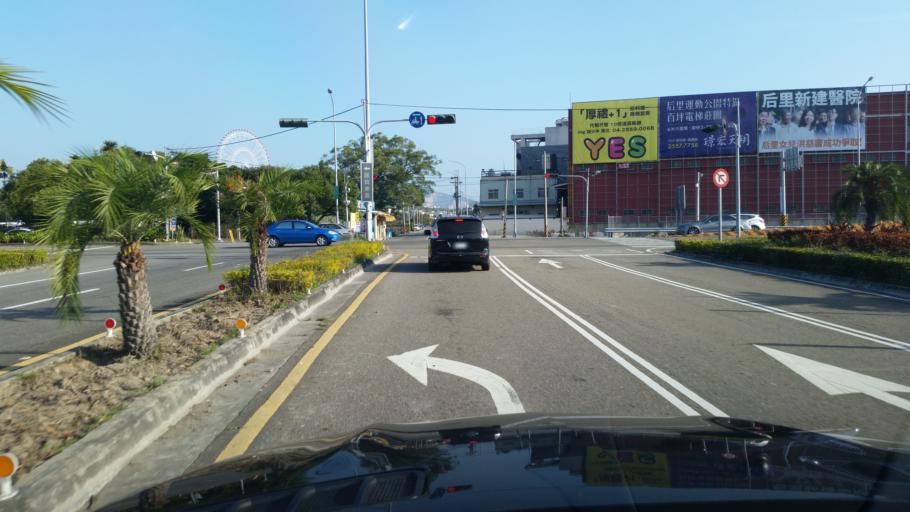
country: TW
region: Taiwan
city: Fengyuan
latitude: 24.3147
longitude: 120.6975
